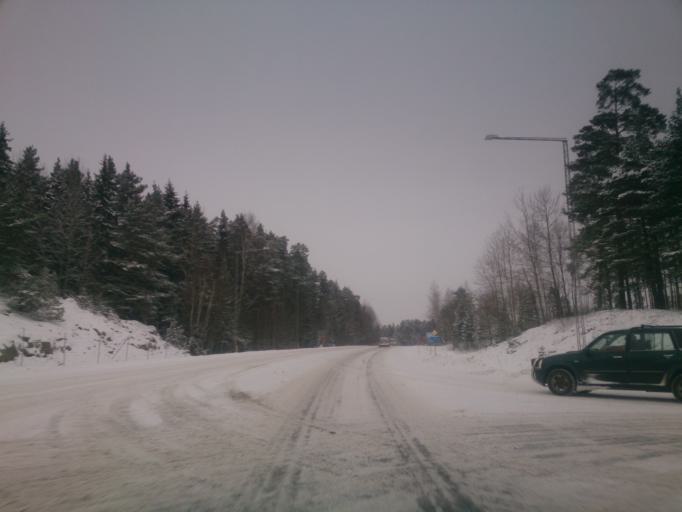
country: SE
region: OEstergoetland
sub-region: Norrkopings Kommun
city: Kimstad
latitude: 58.4916
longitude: 15.9510
